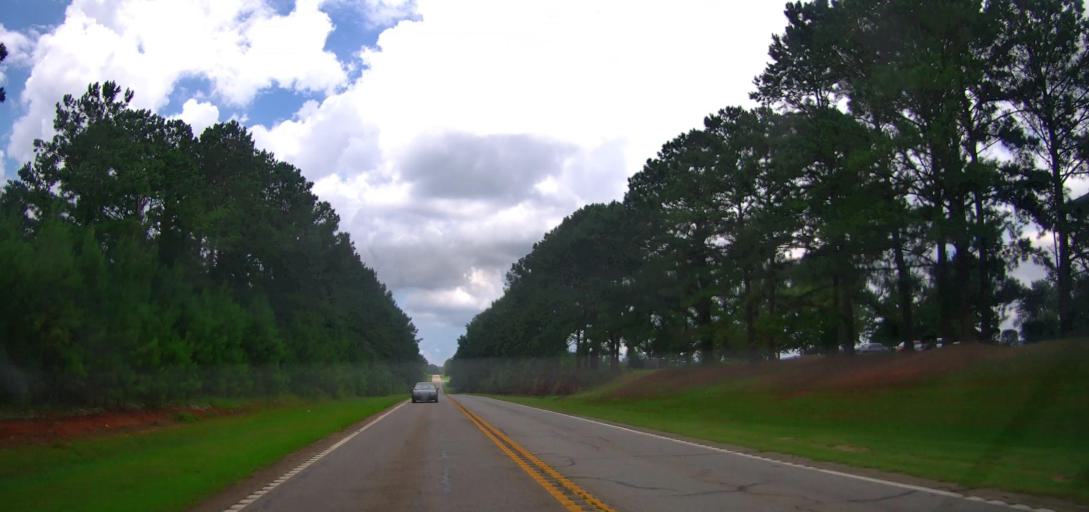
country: US
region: Georgia
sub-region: Pulaski County
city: Hawkinsville
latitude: 32.3243
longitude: -83.5156
